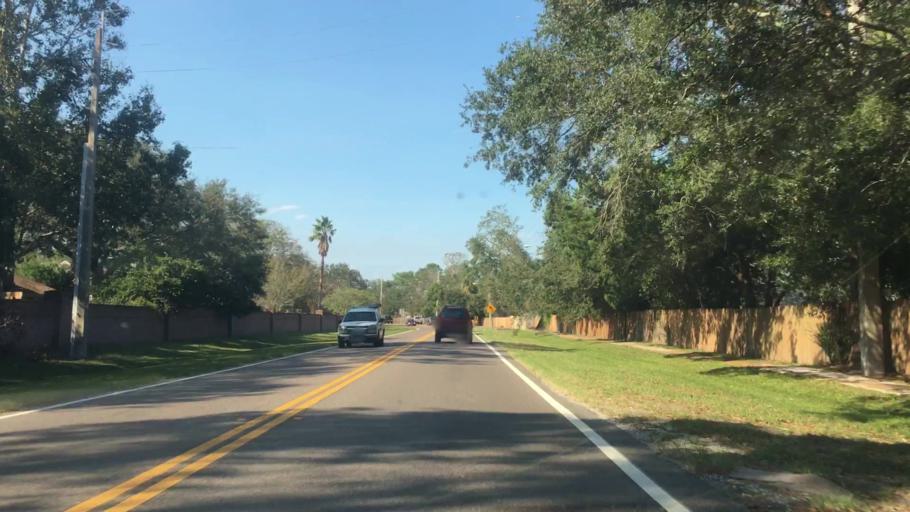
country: US
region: Florida
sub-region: Duval County
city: Neptune Beach
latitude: 30.2965
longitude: -81.4378
